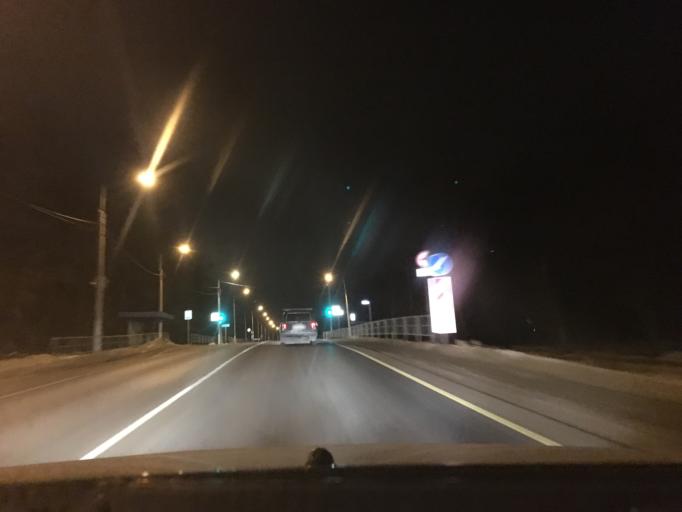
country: RU
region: Tula
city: Pervomayskiy
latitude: 54.0724
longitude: 37.5401
